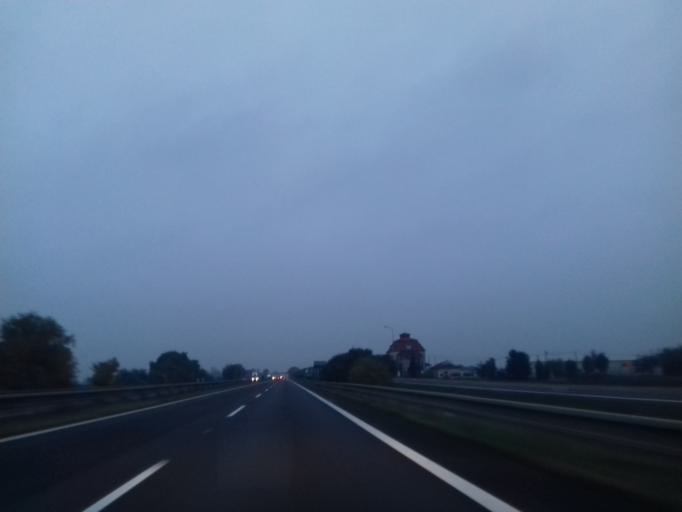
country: CZ
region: Olomoucky
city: Naklo
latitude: 49.6557
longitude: 17.1153
